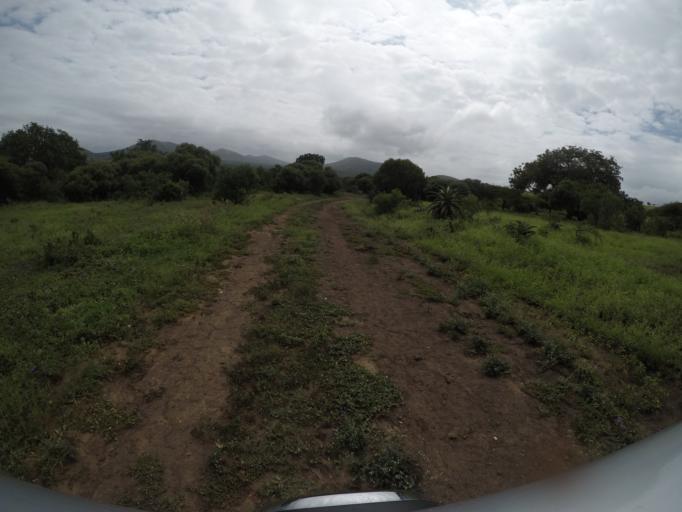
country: ZA
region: KwaZulu-Natal
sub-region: uThungulu District Municipality
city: Empangeni
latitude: -28.6252
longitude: 31.8637
